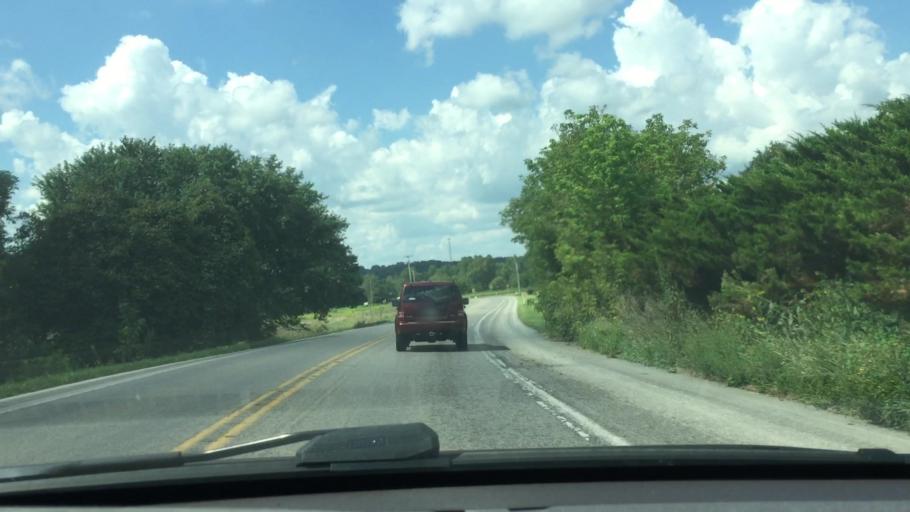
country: US
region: Pennsylvania
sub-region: Lawrence County
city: New Wilmington
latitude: 41.1210
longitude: -80.3136
